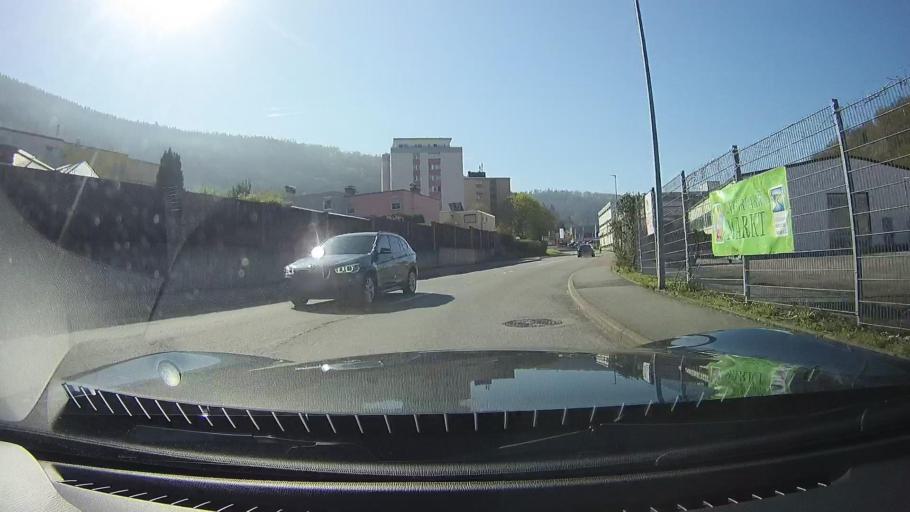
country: DE
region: Baden-Wuerttemberg
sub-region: Karlsruhe Region
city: Eberbach
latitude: 49.4730
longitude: 8.9942
